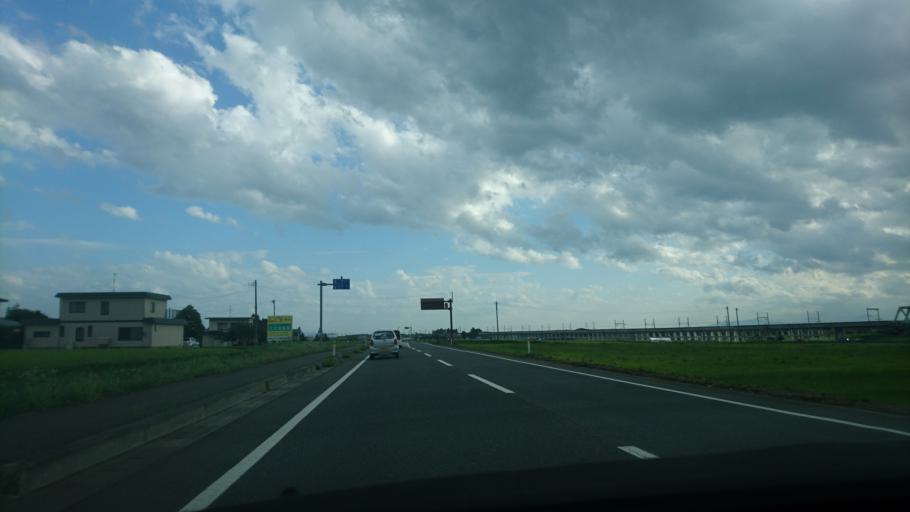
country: JP
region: Iwate
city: Kitakami
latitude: 39.2467
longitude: 141.1179
